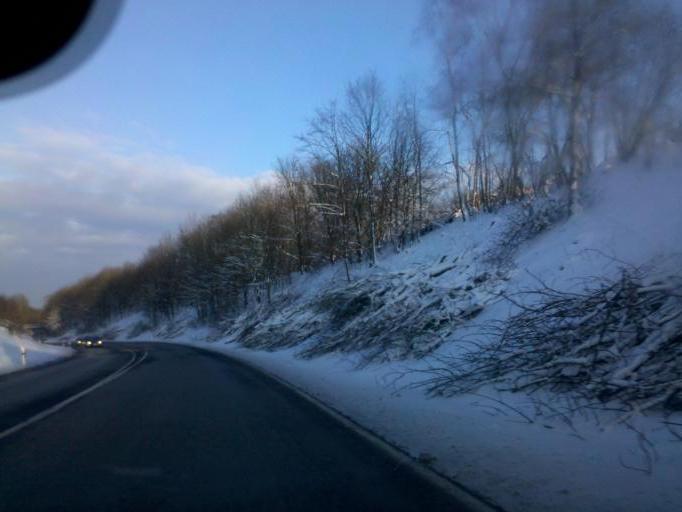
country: DE
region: North Rhine-Westphalia
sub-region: Regierungsbezirk Arnsberg
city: Drolshagen
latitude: 51.0540
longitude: 7.7577
